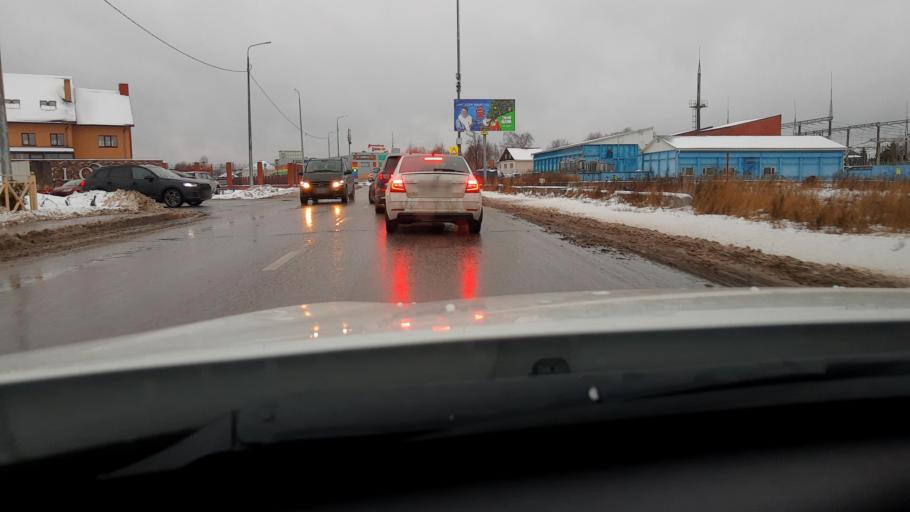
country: RU
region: Moskovskaya
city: Krasnogorsk
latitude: 55.8607
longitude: 37.3266
